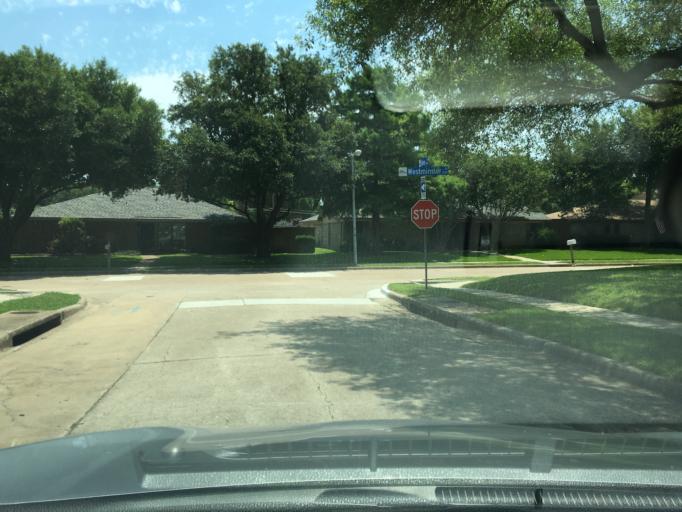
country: US
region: Texas
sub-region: Dallas County
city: Richardson
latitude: 32.9646
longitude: -96.6878
